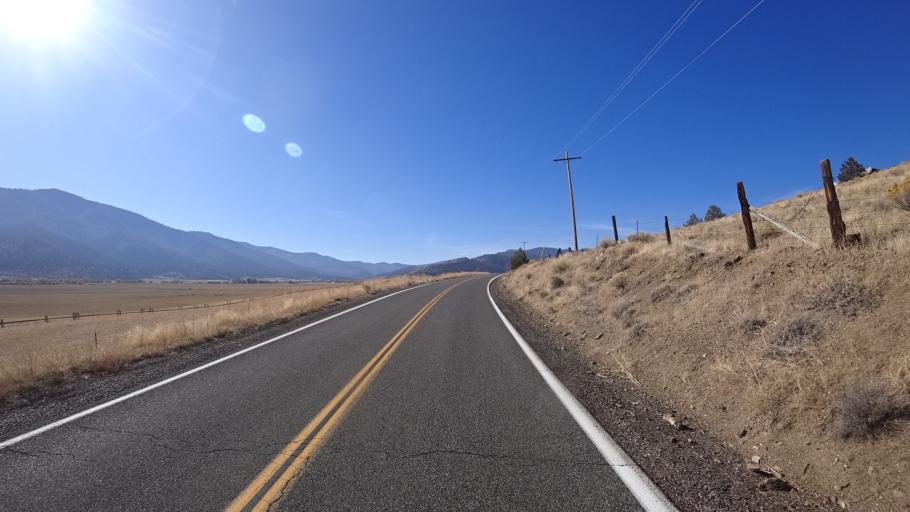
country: US
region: California
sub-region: Siskiyou County
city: Weed
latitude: 41.5082
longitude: -122.5339
